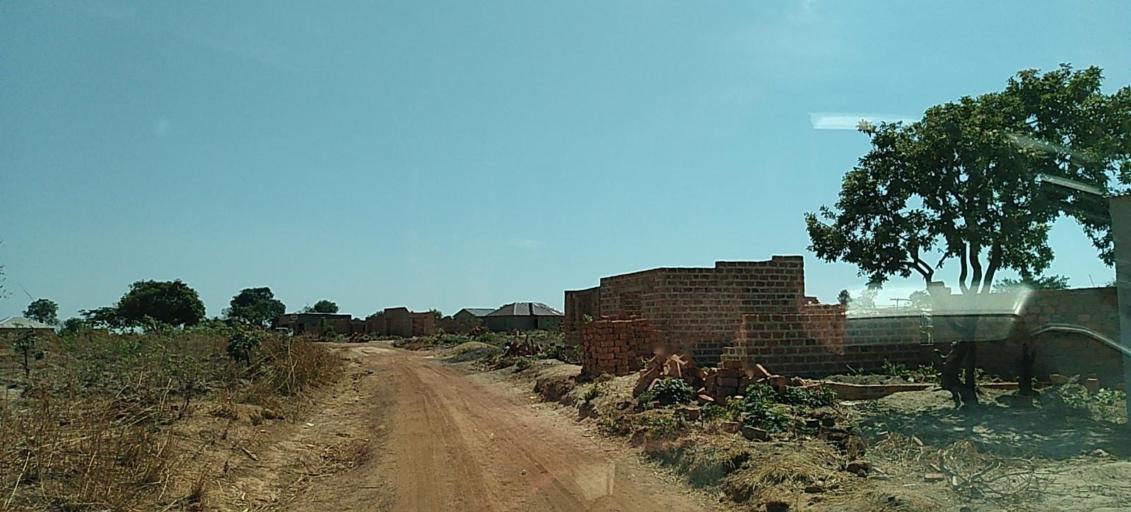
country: ZM
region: Copperbelt
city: Chililabombwe
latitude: -12.3197
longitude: 27.8616
